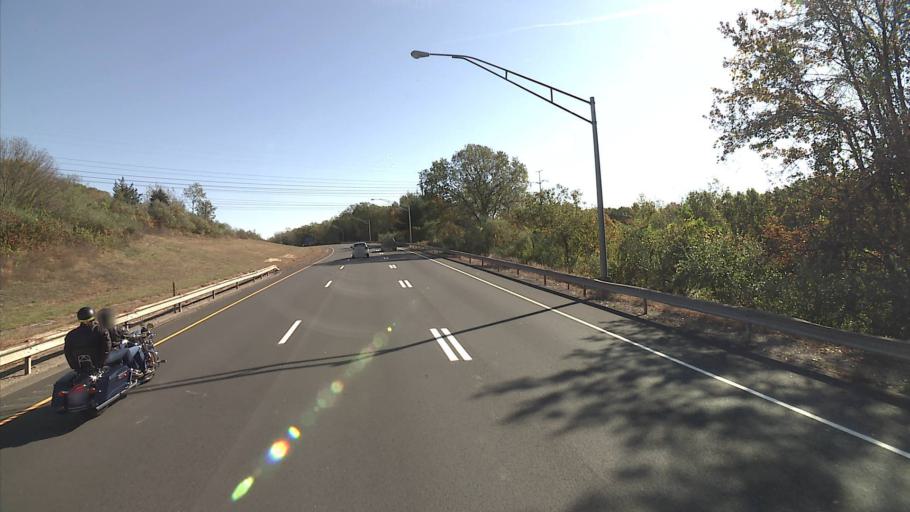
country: US
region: Connecticut
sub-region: Tolland County
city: Mansfield City
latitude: 41.7218
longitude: -72.2703
